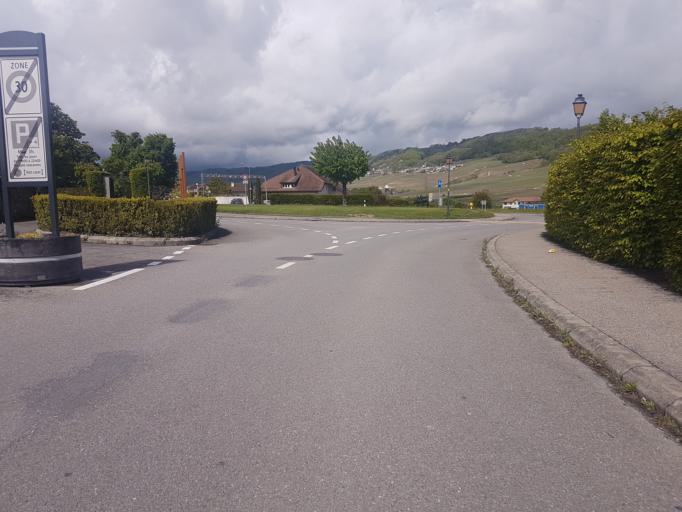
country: CH
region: Vaud
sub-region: Nyon District
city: Perroy
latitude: 46.4679
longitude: 6.3626
